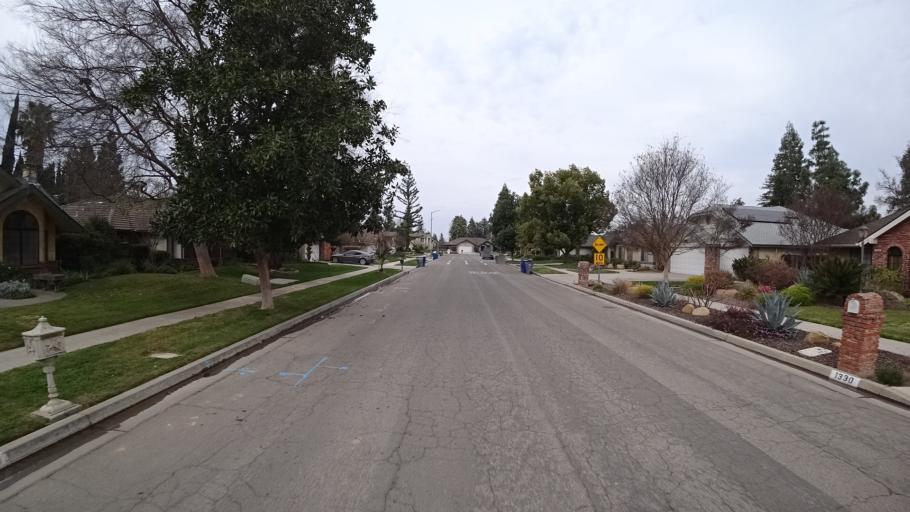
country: US
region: California
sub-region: Fresno County
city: Clovis
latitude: 36.8470
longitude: -119.7596
